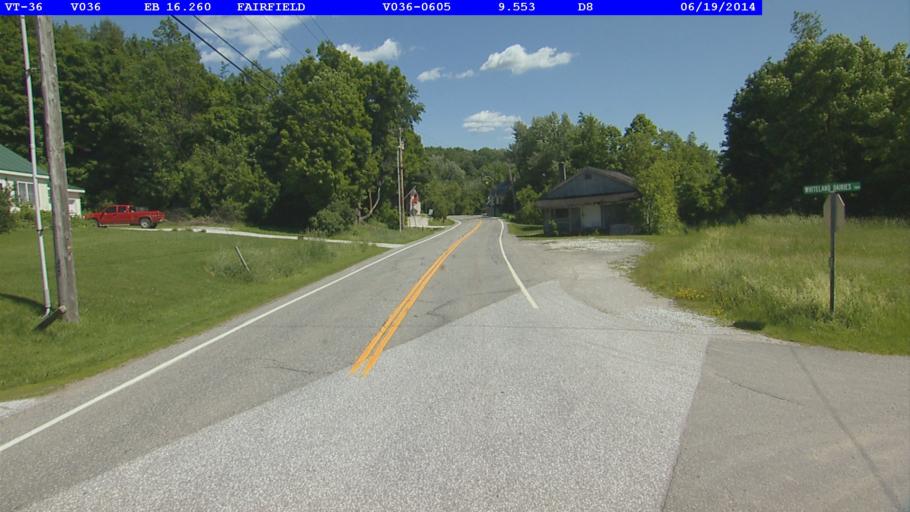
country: US
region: Vermont
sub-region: Franklin County
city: Enosburg Falls
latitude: 44.7840
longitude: -72.8574
